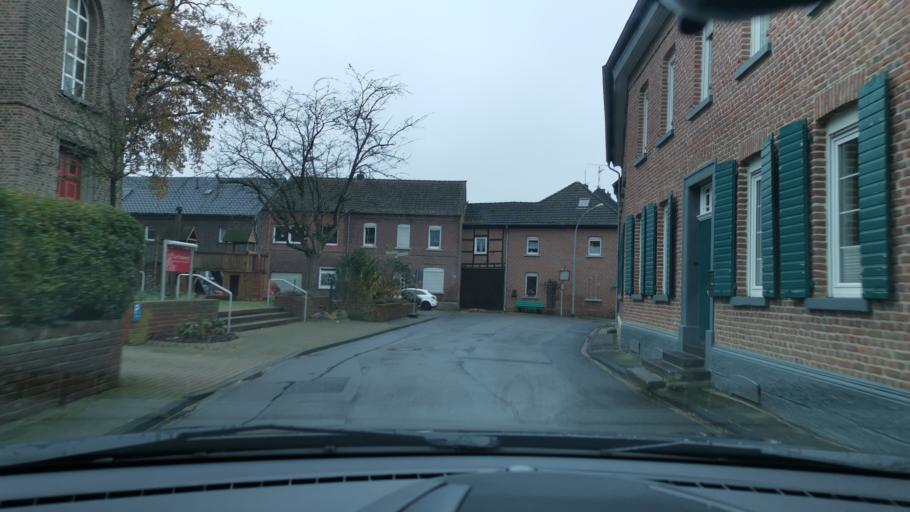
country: DE
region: North Rhine-Westphalia
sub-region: Regierungsbezirk Dusseldorf
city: Juchen
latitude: 51.1151
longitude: 6.5044
